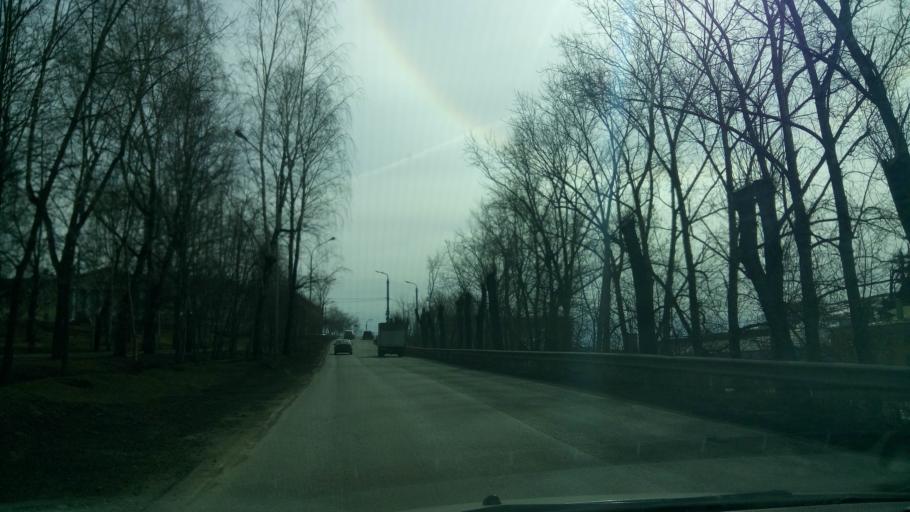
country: RU
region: Sverdlovsk
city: Nizhniy Tagil
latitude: 57.9065
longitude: 59.9476
